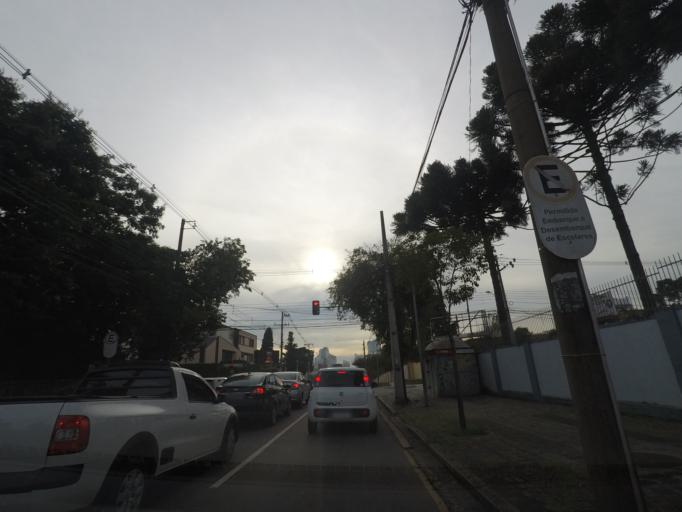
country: BR
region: Parana
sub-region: Curitiba
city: Curitiba
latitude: -25.4391
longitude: -49.2915
